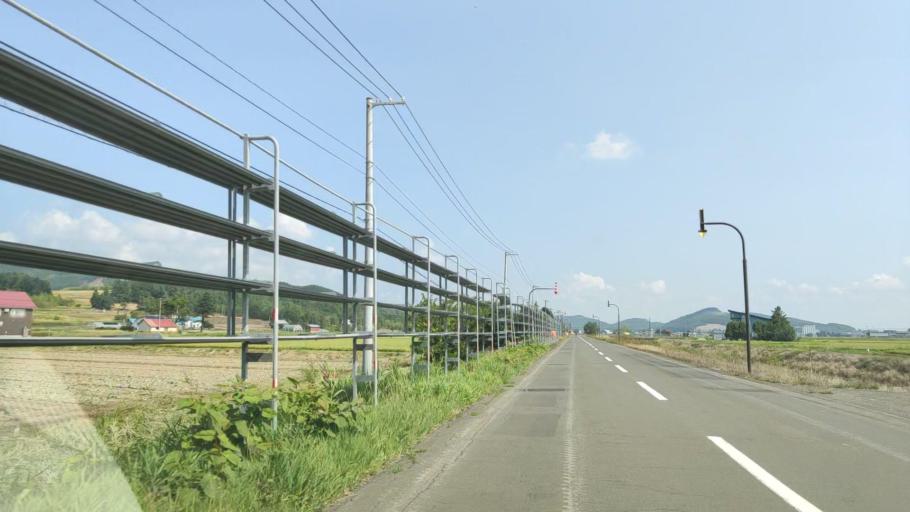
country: JP
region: Hokkaido
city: Shimo-furano
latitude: 43.3737
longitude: 142.3887
